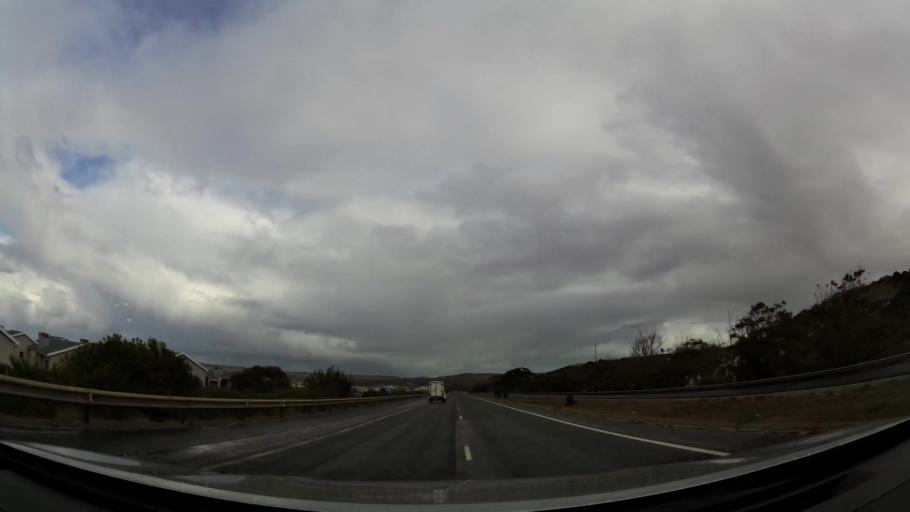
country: ZA
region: Western Cape
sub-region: Eden District Municipality
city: Mossel Bay
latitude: -34.1344
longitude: 22.1019
